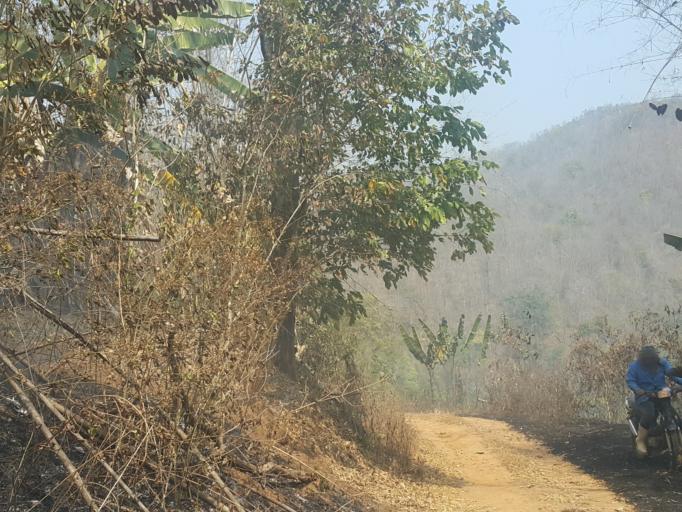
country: TH
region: Chiang Mai
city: Hang Dong
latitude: 18.7519
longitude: 98.8269
